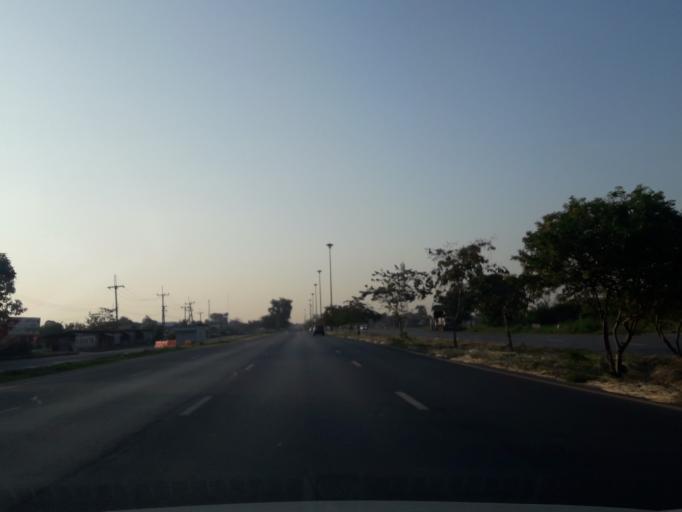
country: TH
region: Phra Nakhon Si Ayutthaya
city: Bang Pa-in
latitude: 14.2022
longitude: 100.5494
